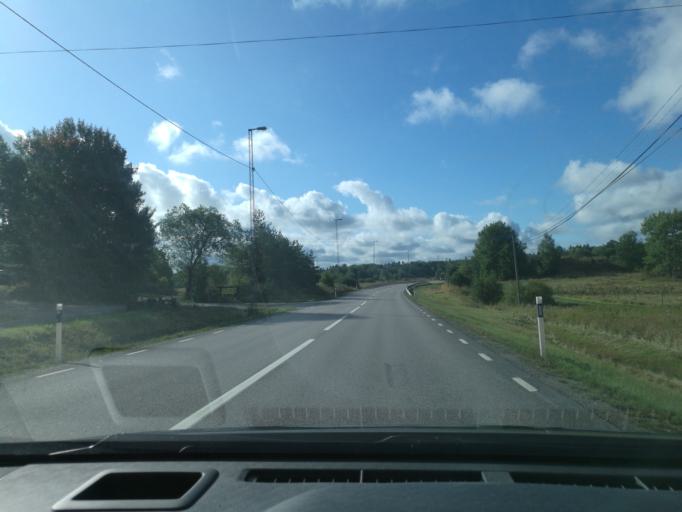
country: SE
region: Stockholm
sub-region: Upplands Vasby Kommun
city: Upplands Vaesby
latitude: 59.5371
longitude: 17.9929
